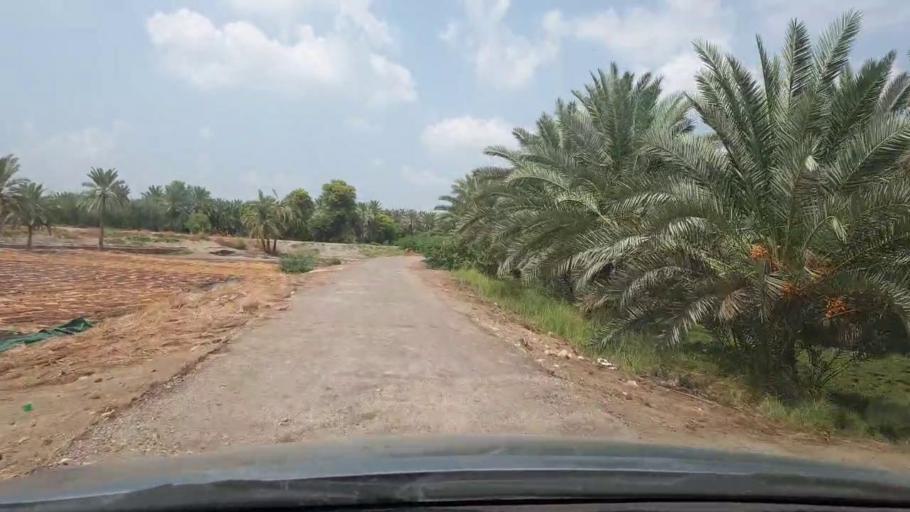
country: PK
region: Sindh
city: Kot Diji
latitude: 27.3947
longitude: 68.7409
